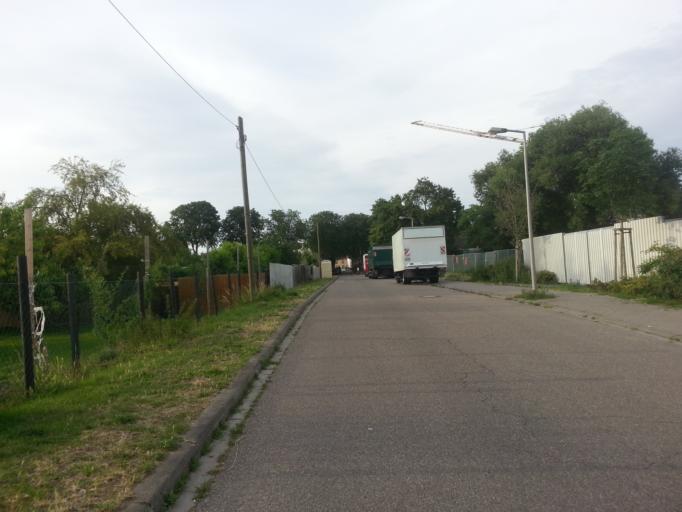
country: DE
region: Rheinland-Pfalz
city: Altrip
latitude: 49.4487
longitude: 8.4875
